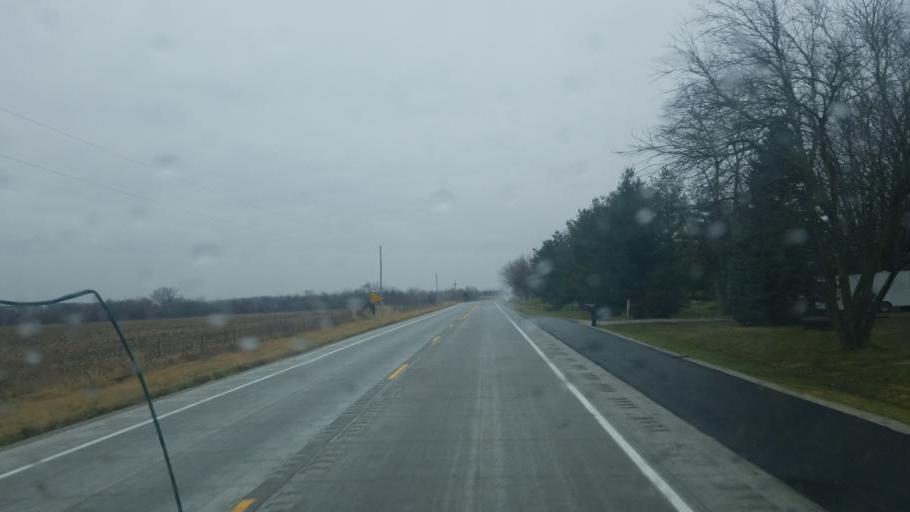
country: US
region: Indiana
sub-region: Shelby County
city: Shelbyville
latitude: 39.4594
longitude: -85.7608
